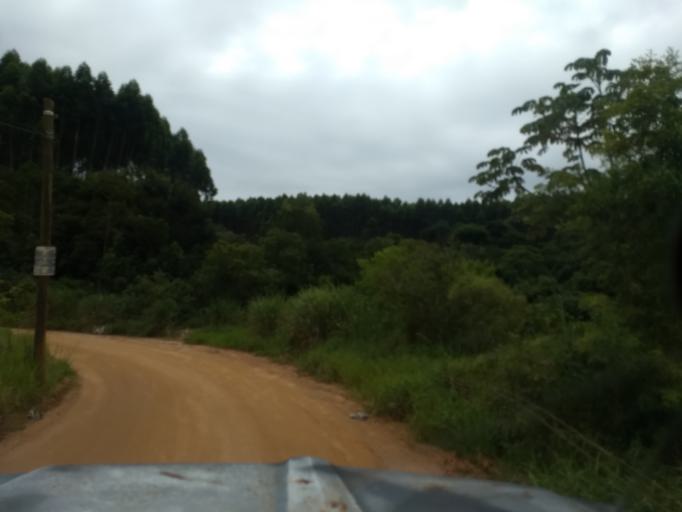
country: BR
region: Sao Paulo
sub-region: Cabreuva
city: Cabreuva
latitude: -23.3909
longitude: -47.1950
